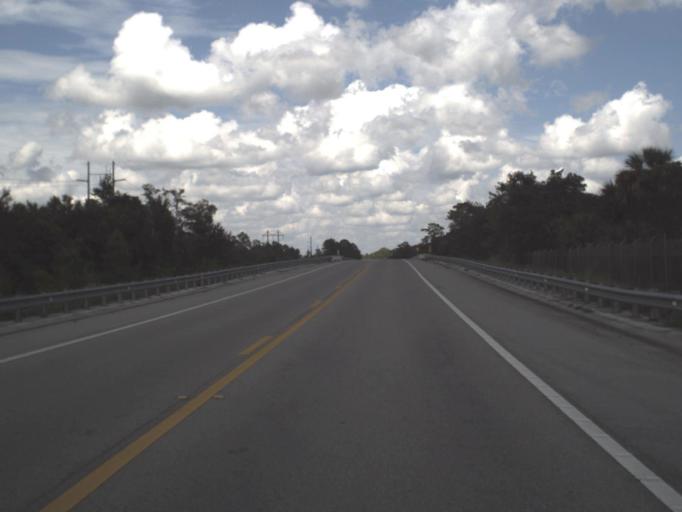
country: US
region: Florida
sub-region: Collier County
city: Immokalee
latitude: 26.2444
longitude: -81.3423
